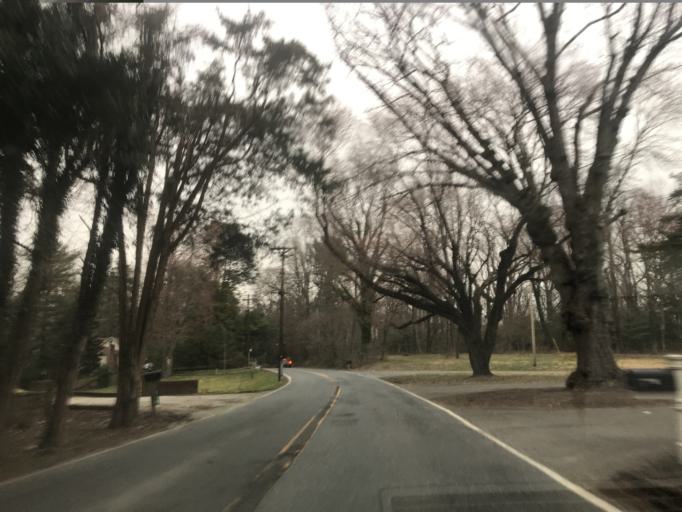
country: US
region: Maryland
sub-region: Anne Arundel County
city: Cape Saint Claire
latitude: 39.0230
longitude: -76.4694
